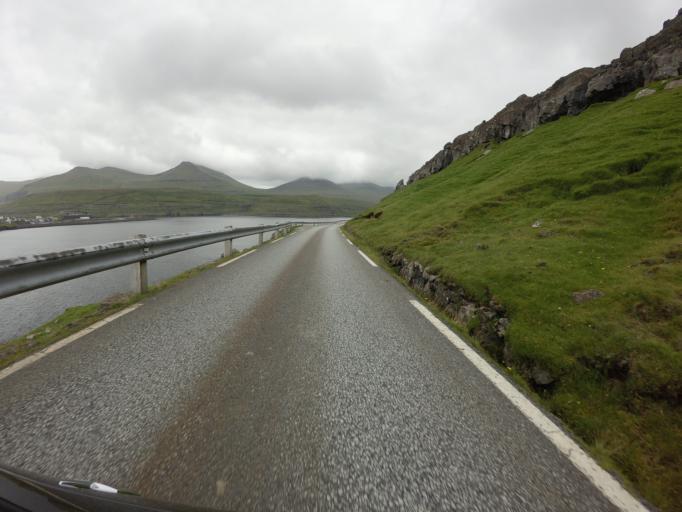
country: FO
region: Eysturoy
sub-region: Eidi
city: Eidi
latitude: 62.2926
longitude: -7.1152
